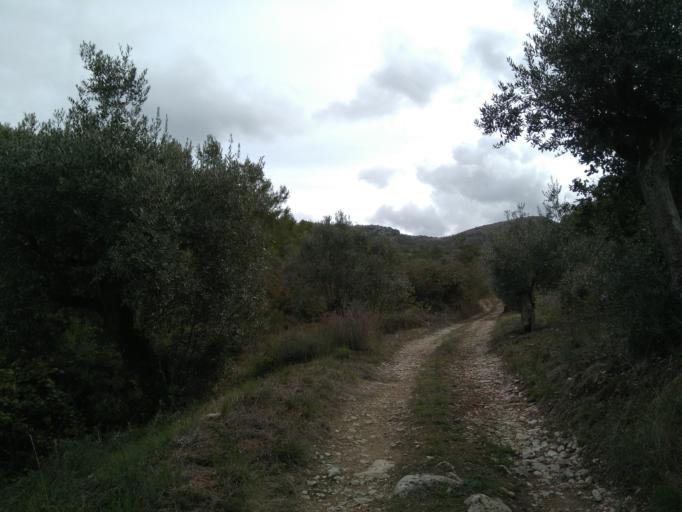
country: PT
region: Leiria
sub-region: Porto de Mos
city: Porto de Mos
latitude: 39.5807
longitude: -8.8169
